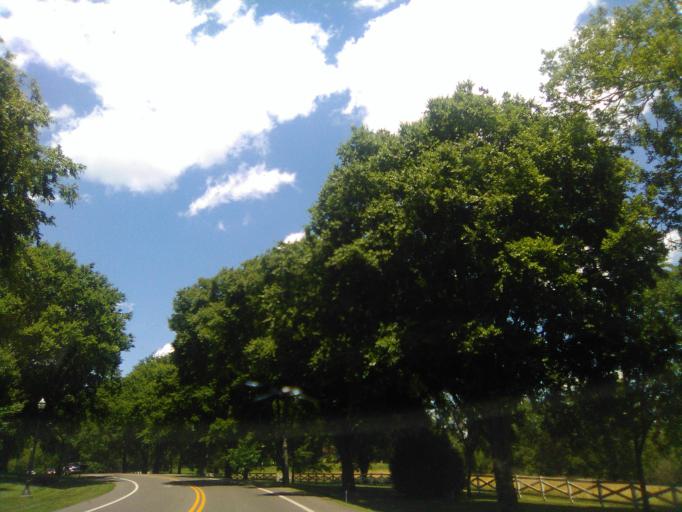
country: US
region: Tennessee
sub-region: Davidson County
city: Belle Meade
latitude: 36.1182
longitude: -86.8601
